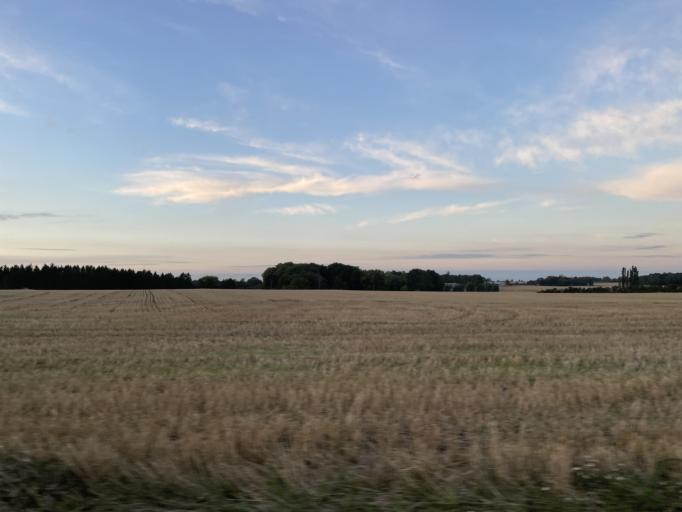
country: DK
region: South Denmark
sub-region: Nyborg Kommune
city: Nyborg
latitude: 55.3534
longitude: 10.7478
